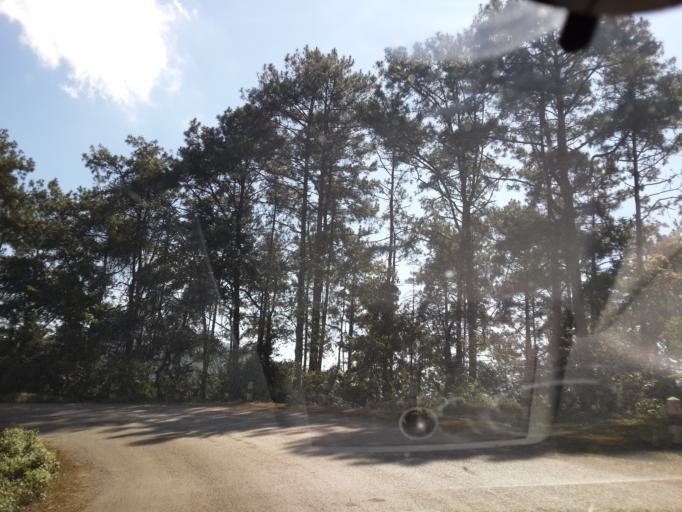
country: TH
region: Chiang Mai
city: Fang
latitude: 19.9130
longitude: 99.0507
